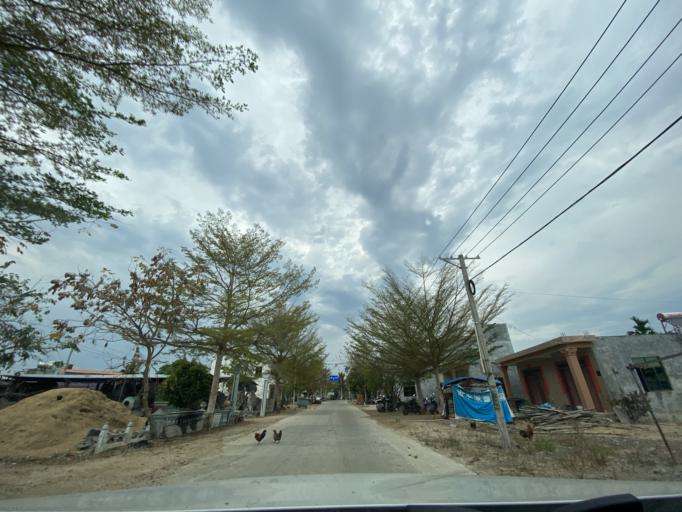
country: CN
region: Hainan
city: Yingzhou
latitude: 18.4225
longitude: 109.8213
